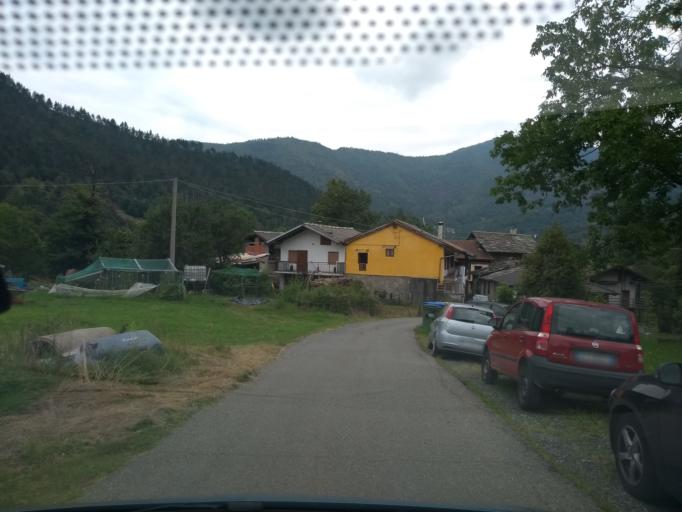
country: IT
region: Piedmont
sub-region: Provincia di Torino
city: La Villa
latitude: 45.2352
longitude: 7.4243
